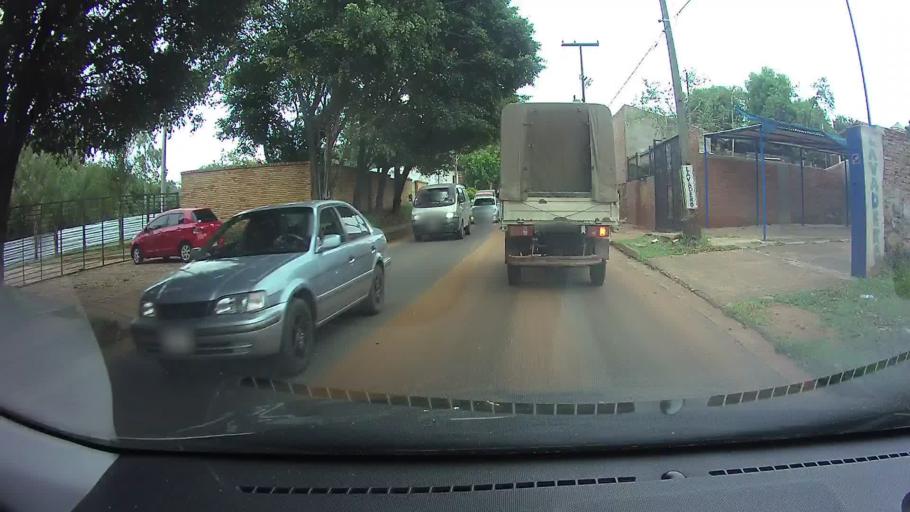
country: PY
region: Central
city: San Lorenzo
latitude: -25.3100
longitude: -57.4915
